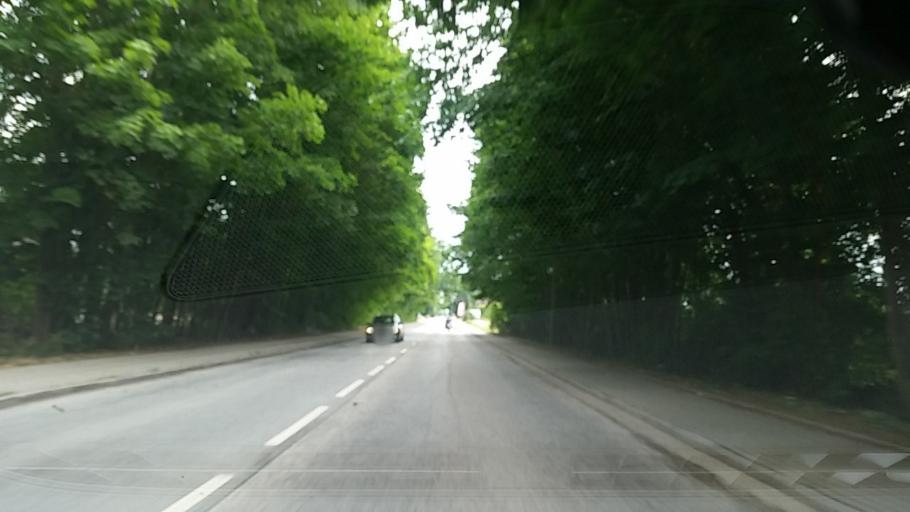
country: DE
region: Hamburg
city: Lemsahl-Mellingstedt
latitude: 53.7004
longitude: 10.0551
